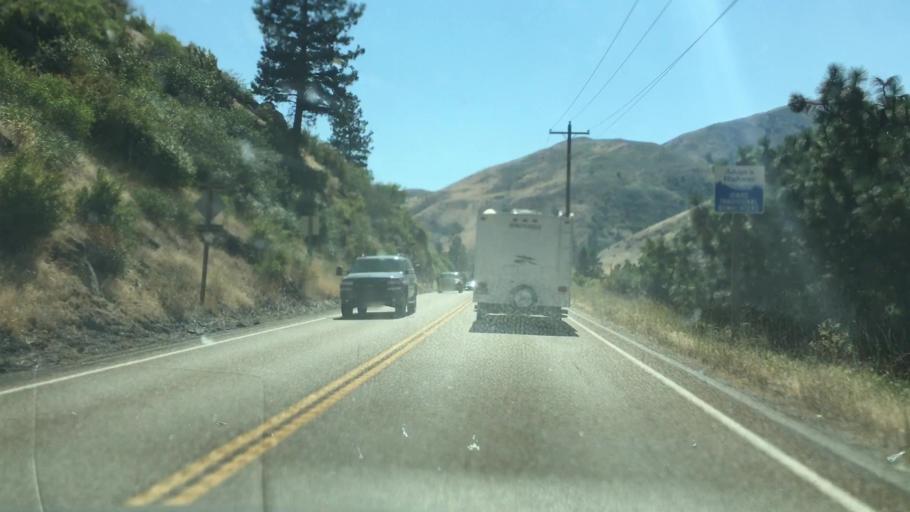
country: US
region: Idaho
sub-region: Boise County
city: Idaho City
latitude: 44.0251
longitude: -116.1420
